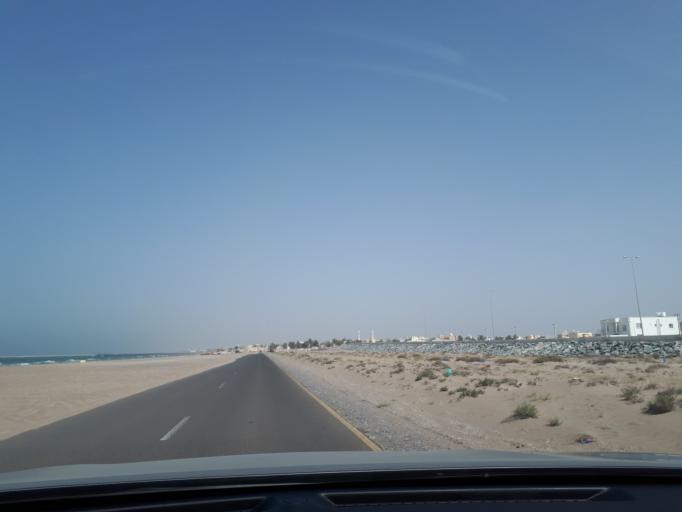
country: OM
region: Al Batinah
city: Barka'
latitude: 23.7134
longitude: 57.8742
